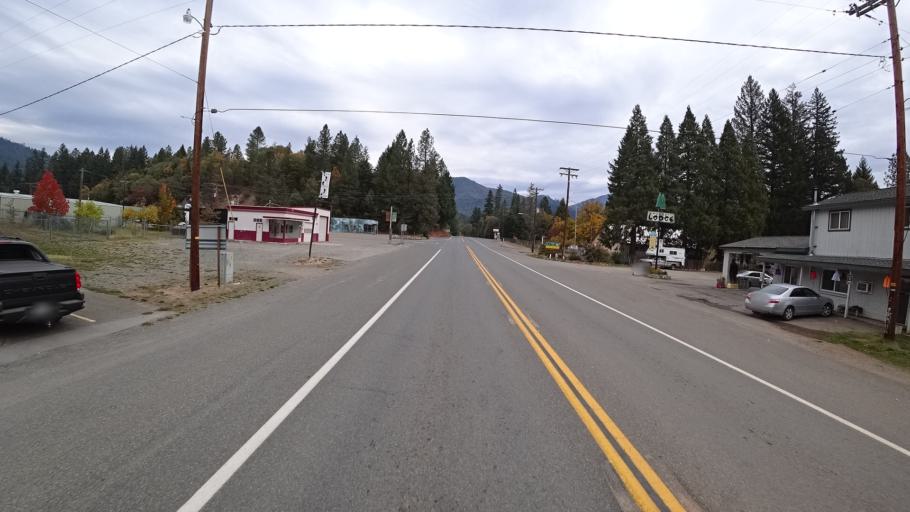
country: US
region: California
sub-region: Siskiyou County
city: Happy Camp
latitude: 41.7980
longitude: -123.3748
